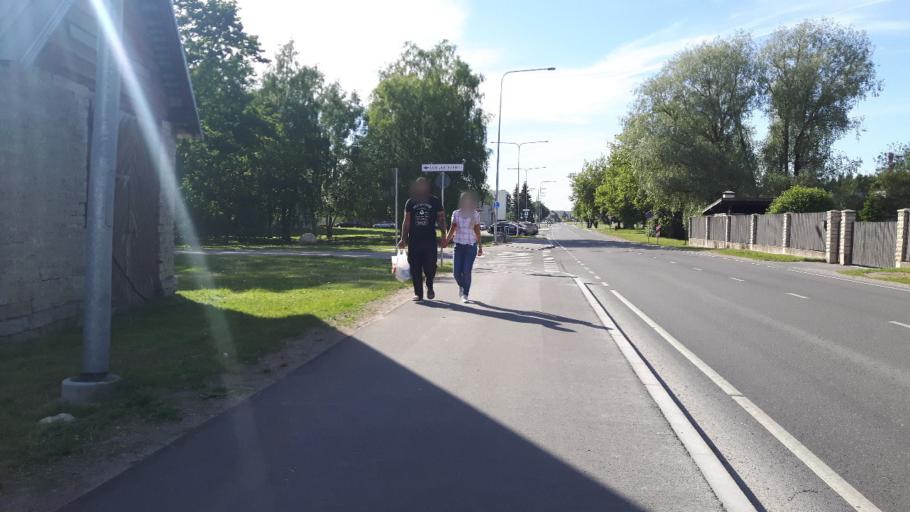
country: EE
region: Harju
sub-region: Joelaehtme vald
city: Loo
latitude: 59.4333
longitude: 24.9493
